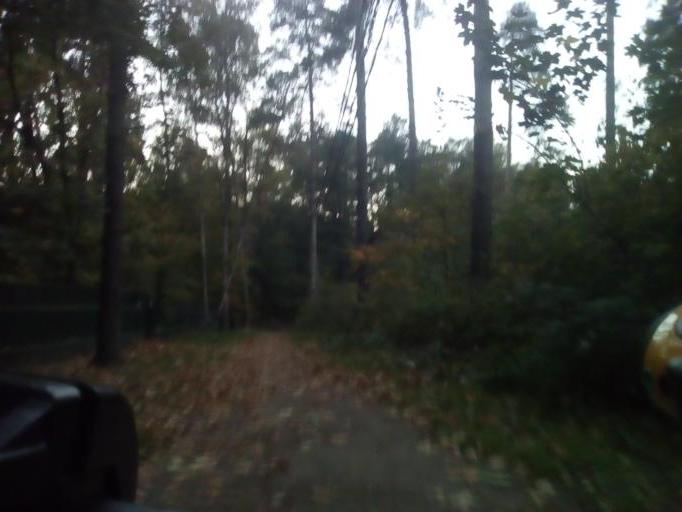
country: RU
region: Moskovskaya
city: Kratovo
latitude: 55.5989
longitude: 38.1550
